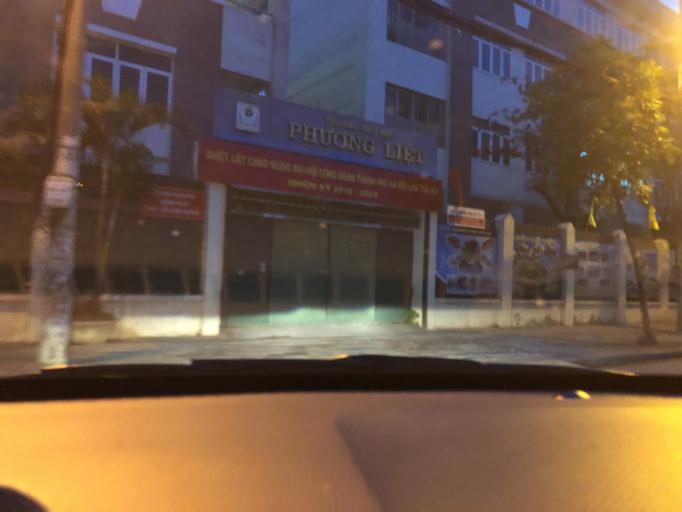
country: VN
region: Ha Noi
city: Hai BaTrung
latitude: 20.9969
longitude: 105.8386
